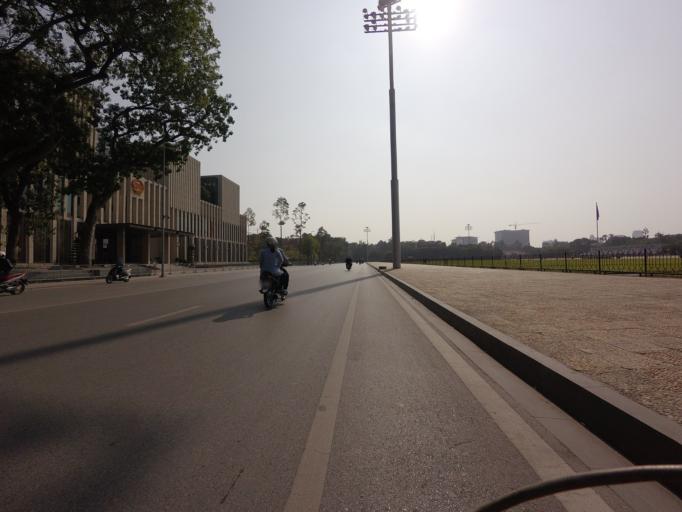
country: VN
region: Ha Noi
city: Hanoi
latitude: 21.0377
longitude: 105.8367
